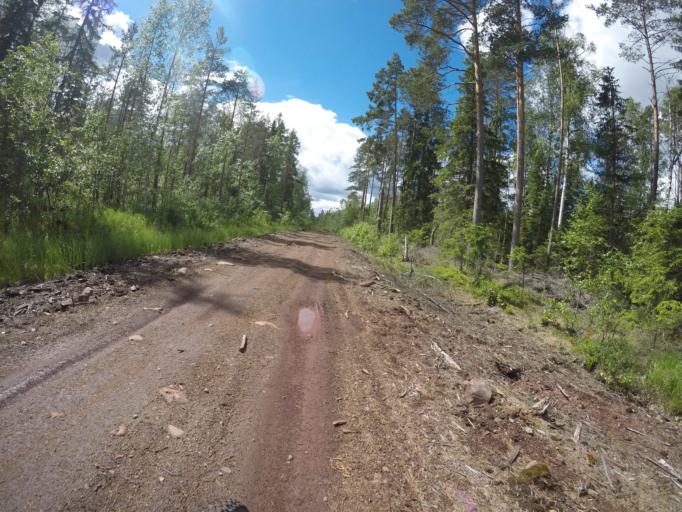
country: SE
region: Vaermland
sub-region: Filipstads Kommun
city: Lesjofors
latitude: 60.1379
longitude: 14.3406
